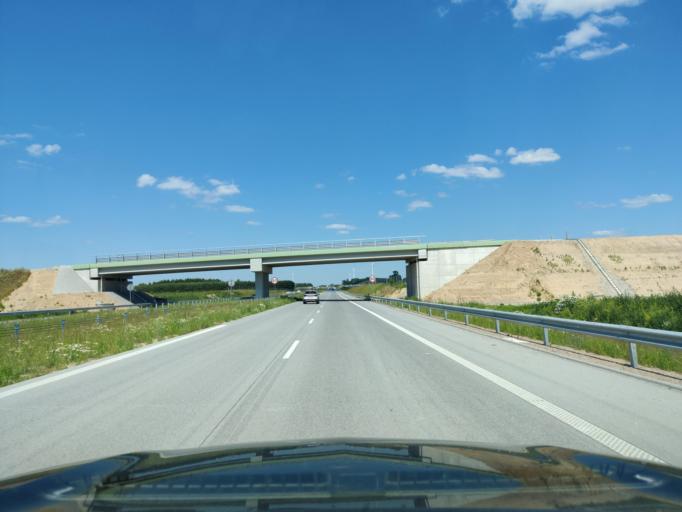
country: PL
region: Masovian Voivodeship
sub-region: Powiat mlawski
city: Wisniewo
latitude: 53.0259
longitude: 20.3461
